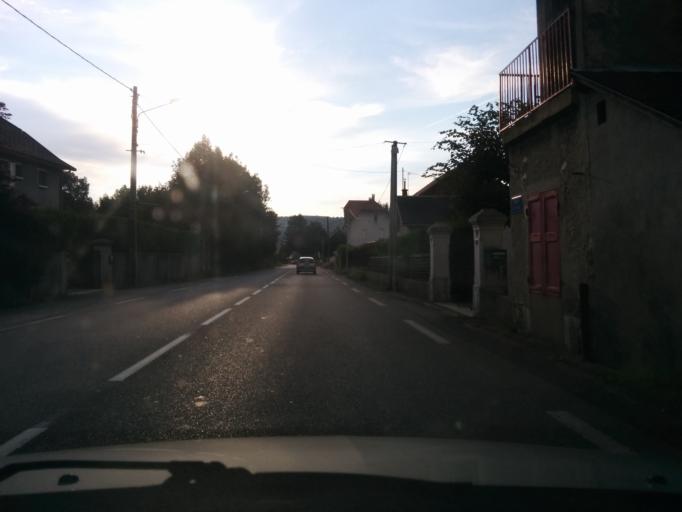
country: FR
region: Rhone-Alpes
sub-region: Departement de l'Isere
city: Saint-Laurent-du-Pont
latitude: 45.3881
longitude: 5.7281
